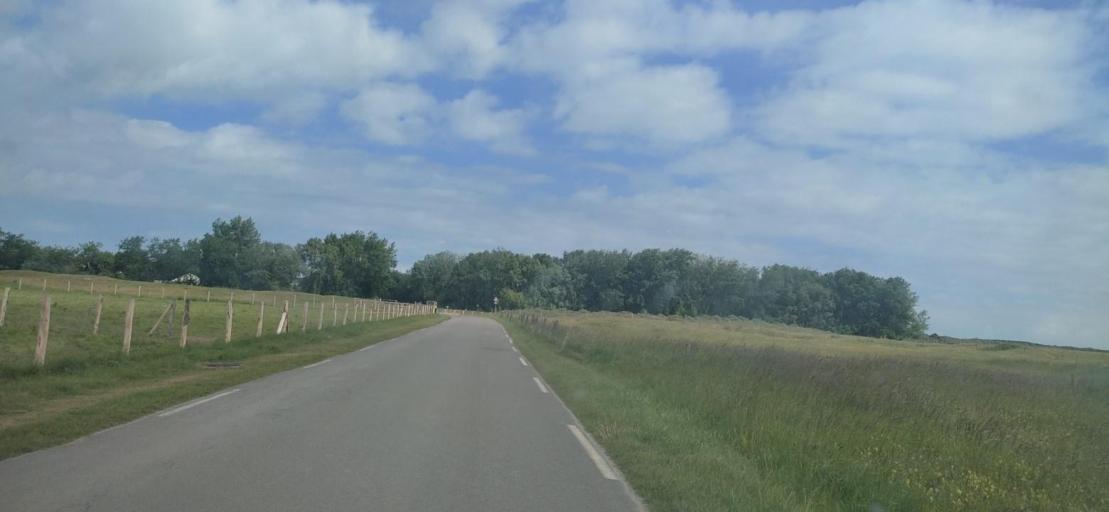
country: FR
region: Nord-Pas-de-Calais
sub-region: Departement du Pas-de-Calais
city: Oye-Plage
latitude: 51.0012
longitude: 2.0685
